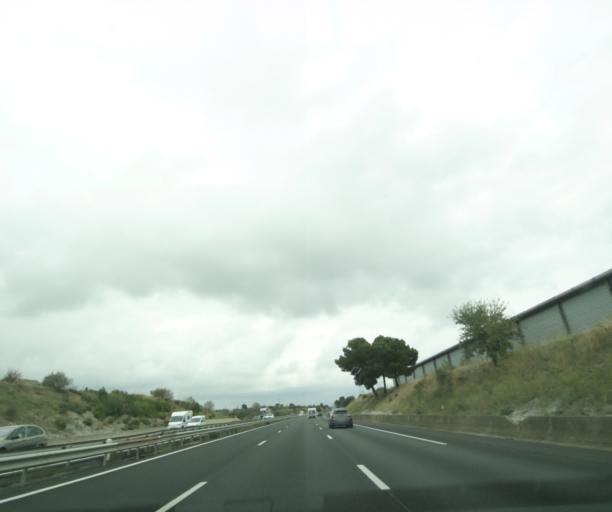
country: FR
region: Languedoc-Roussillon
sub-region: Departement de l'Herault
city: Meze
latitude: 43.4446
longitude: 3.5749
